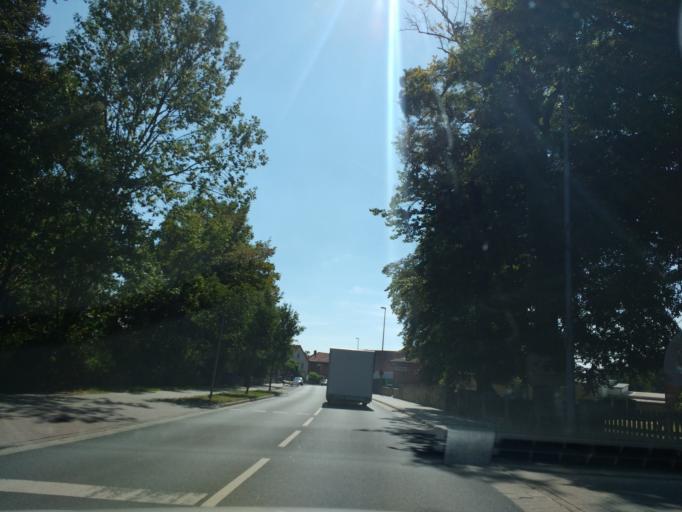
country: DE
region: Lower Saxony
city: Sohlde
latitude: 52.2110
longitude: 10.1891
